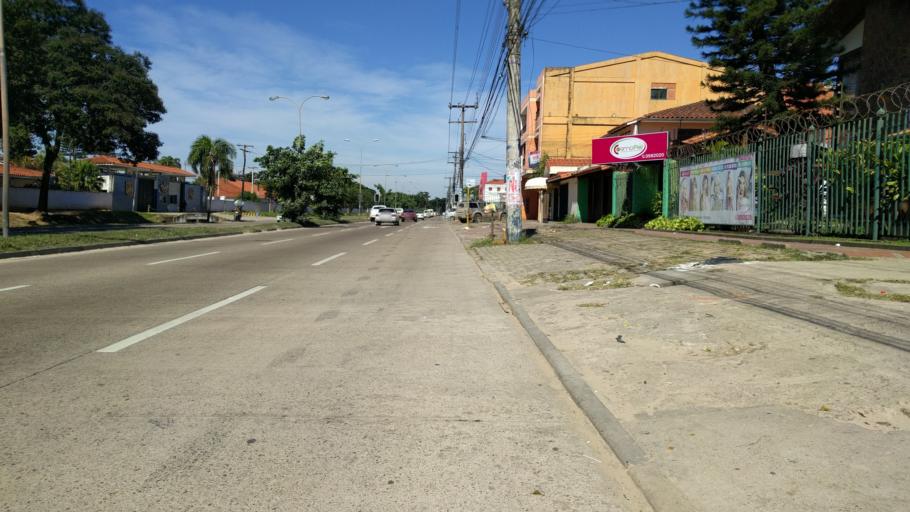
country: BO
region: Santa Cruz
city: Santa Cruz de la Sierra
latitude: -17.8034
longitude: -63.1802
